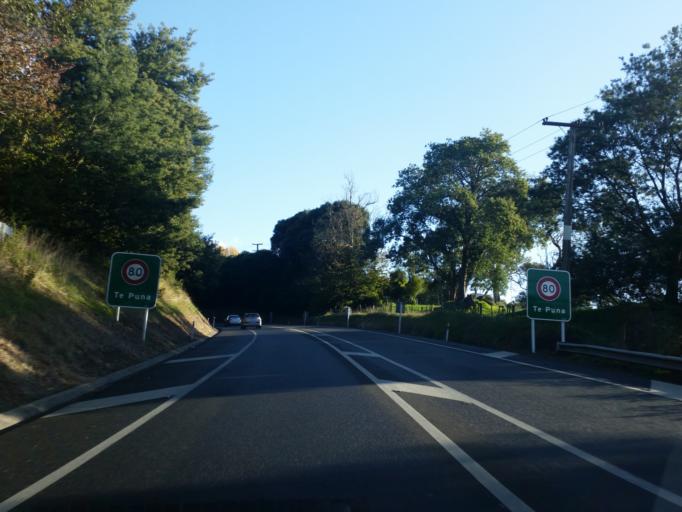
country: NZ
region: Bay of Plenty
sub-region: Tauranga City
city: Tauranga
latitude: -37.6969
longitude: 176.0765
